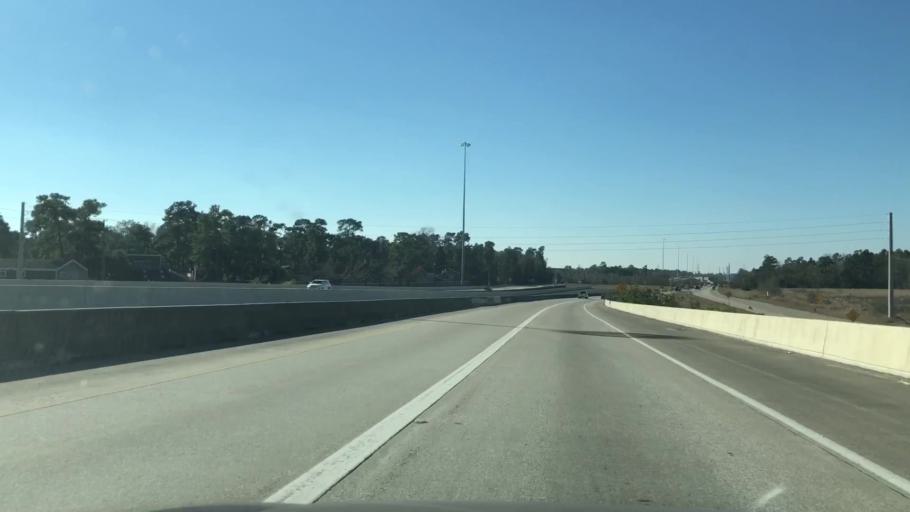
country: US
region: Texas
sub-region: Harris County
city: Cloverleaf
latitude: 29.8150
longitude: -95.2089
